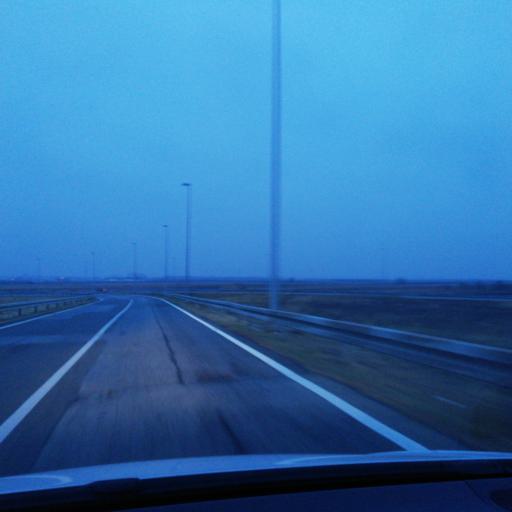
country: RS
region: Autonomna Pokrajina Vojvodina
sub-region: Sremski Okrug
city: Ruma
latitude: 44.9623
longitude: 19.8127
